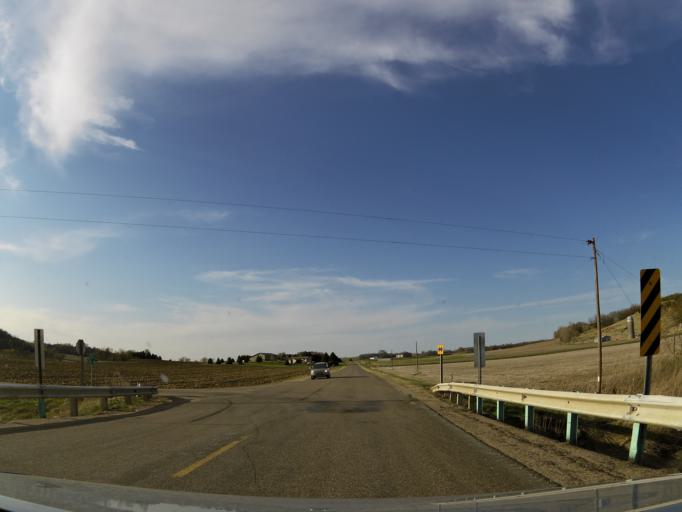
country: US
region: Wisconsin
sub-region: Pierce County
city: River Falls
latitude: 44.7650
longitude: -92.6396
